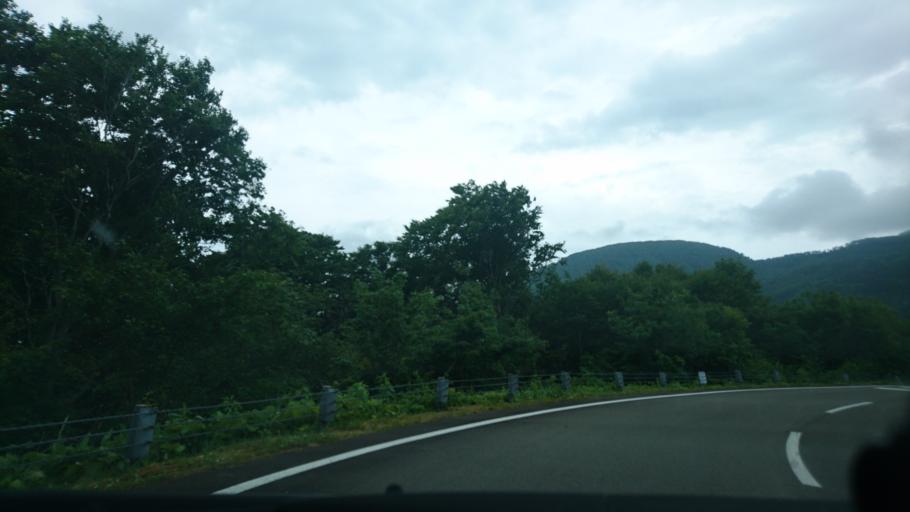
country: JP
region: Akita
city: Yuzawa
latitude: 39.1550
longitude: 140.7510
